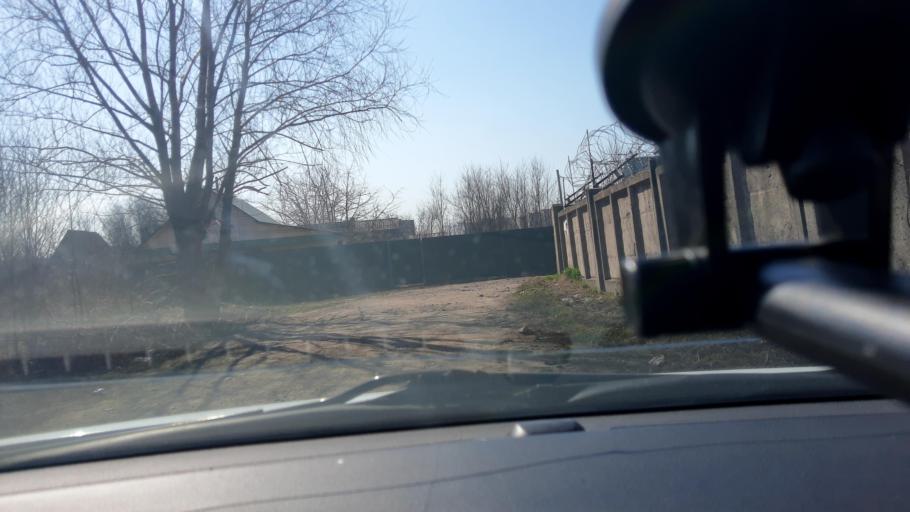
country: RU
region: Bashkortostan
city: Mikhaylovka
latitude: 54.7174
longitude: 55.8222
